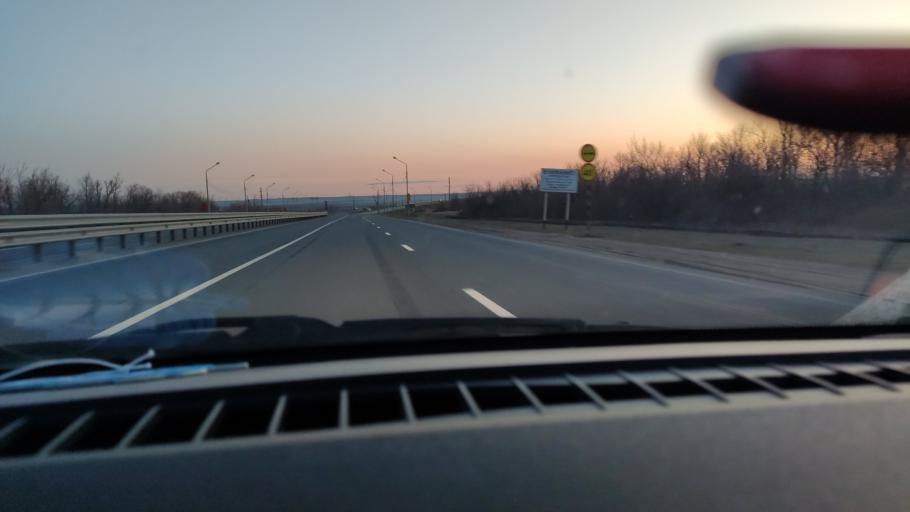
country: RU
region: Saratov
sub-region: Saratovskiy Rayon
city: Saratov
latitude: 51.6626
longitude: 45.9991
